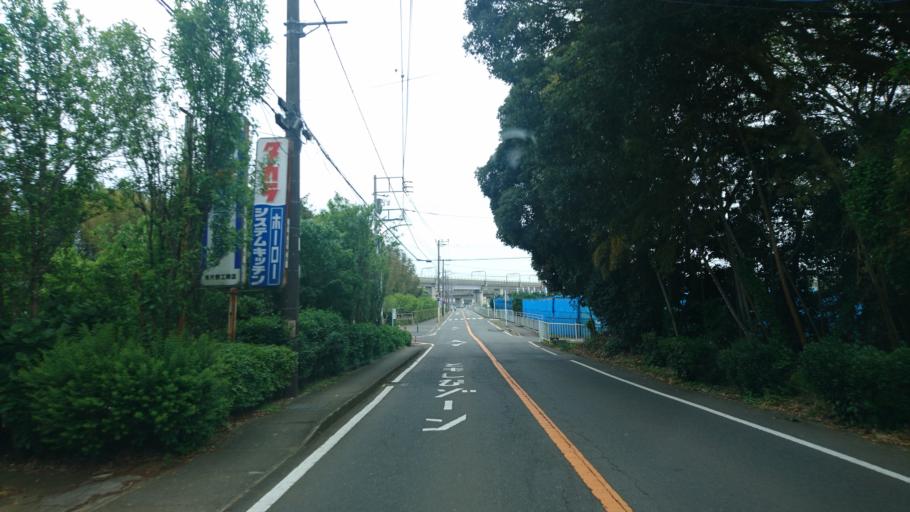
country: JP
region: Kanagawa
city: Fujisawa
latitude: 35.4038
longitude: 139.4781
